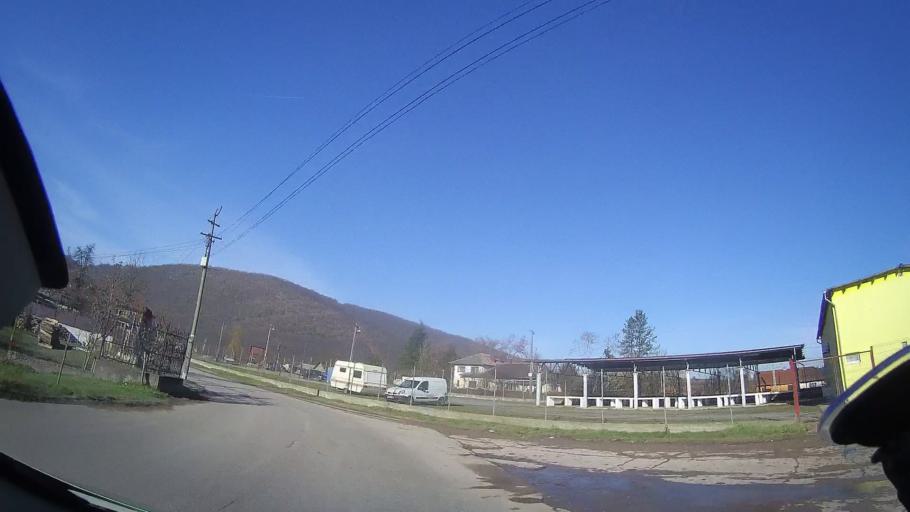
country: RO
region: Bihor
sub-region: Comuna Suncuius
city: Suncuius
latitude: 46.9477
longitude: 22.5375
